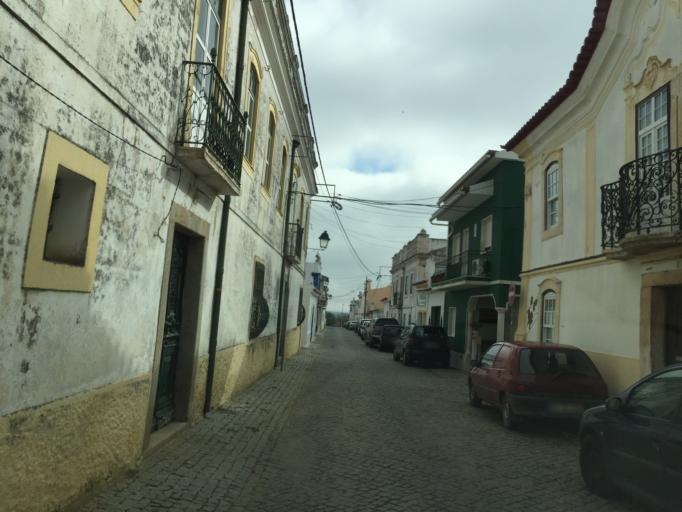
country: PT
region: Portalegre
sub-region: Fronteira
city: Fronteira
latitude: 39.0555
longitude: -7.6467
